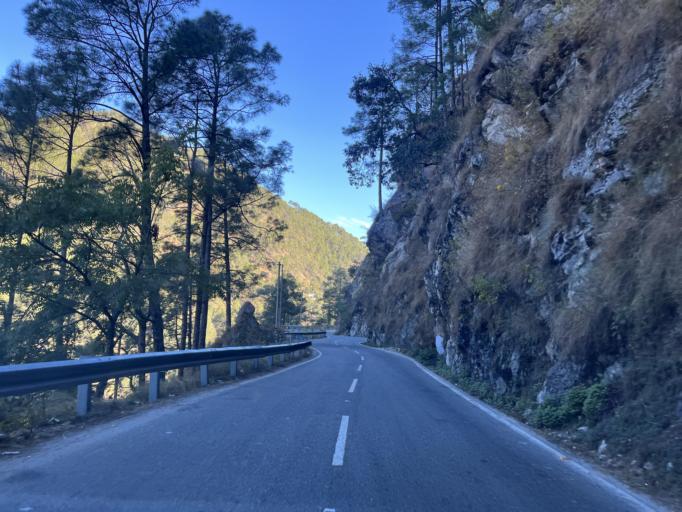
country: IN
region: Uttarakhand
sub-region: Naini Tal
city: Bhowali
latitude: 29.4040
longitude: 79.5103
